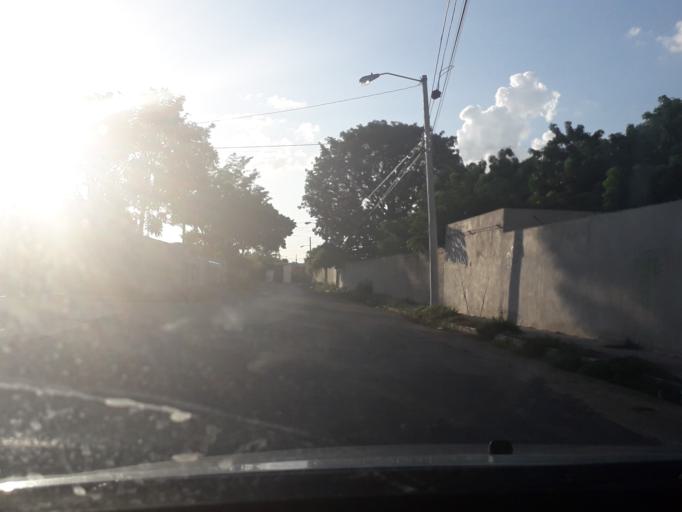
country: MX
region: Yucatan
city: Merida
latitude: 20.9802
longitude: -89.6553
